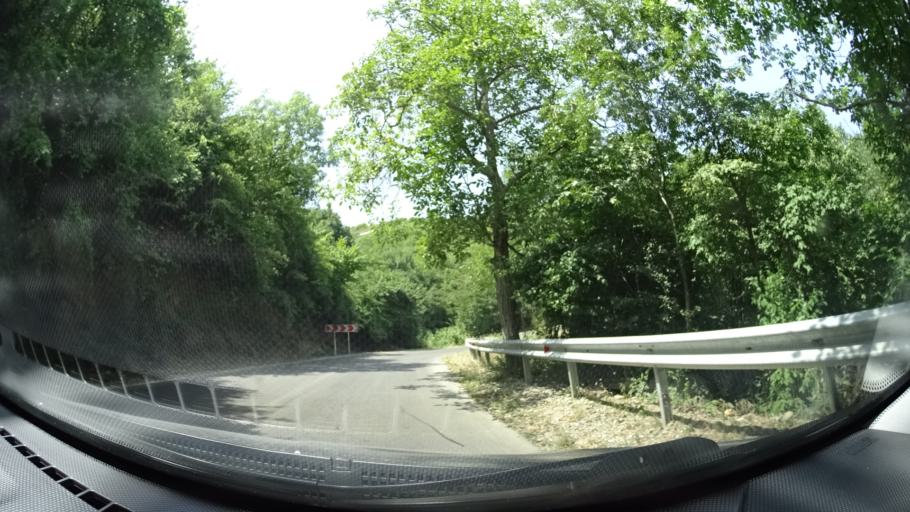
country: GE
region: Kakheti
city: Sighnaghi
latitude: 41.6234
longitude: 45.9348
